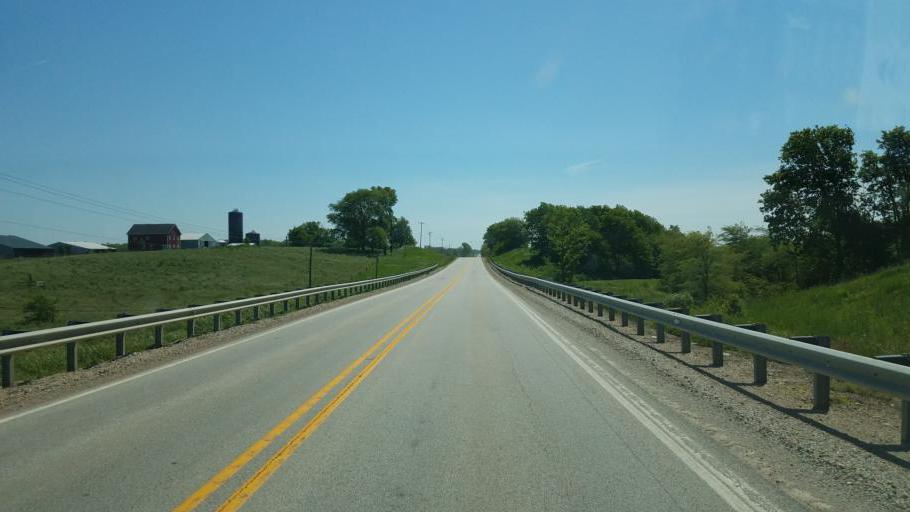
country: US
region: Illinois
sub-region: McLean County
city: Heyworth
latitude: 40.3122
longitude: -89.0302
